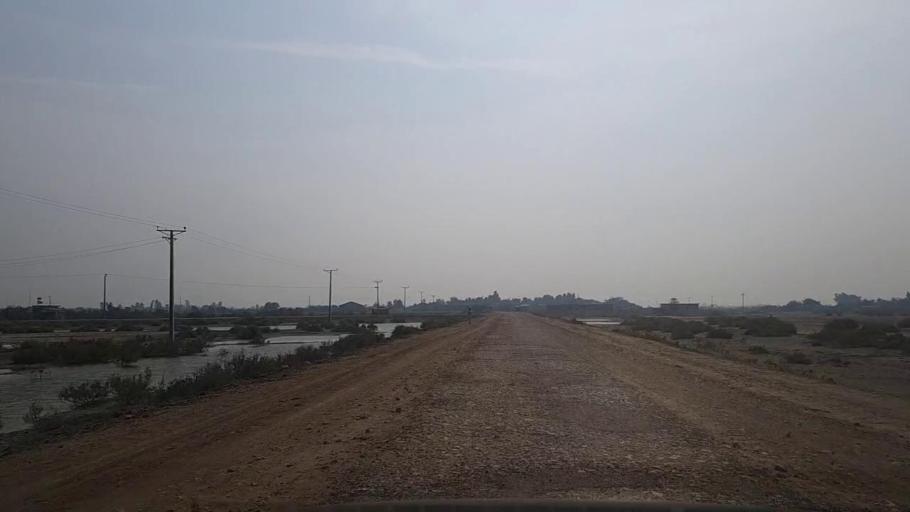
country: PK
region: Sindh
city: Mirpur Sakro
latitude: 24.4055
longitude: 67.7435
